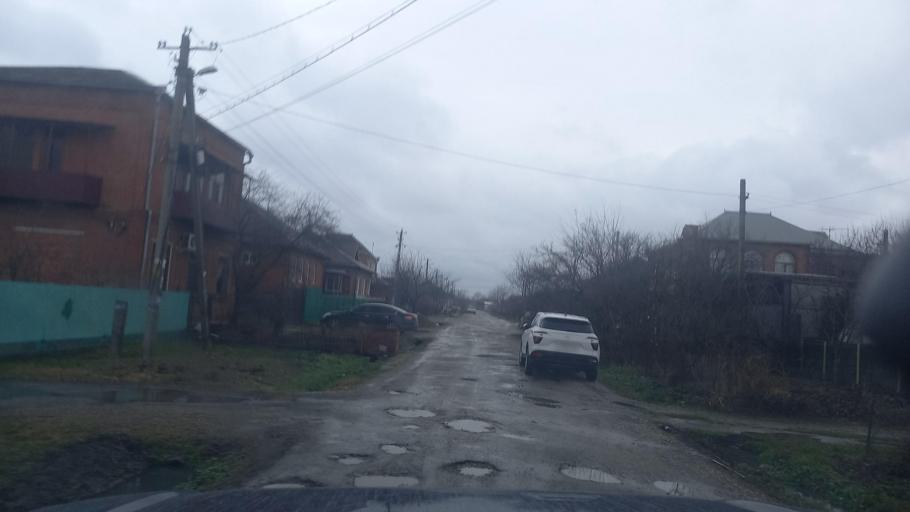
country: RU
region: Adygeya
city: Yablonovskiy
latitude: 44.9869
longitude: 38.9334
